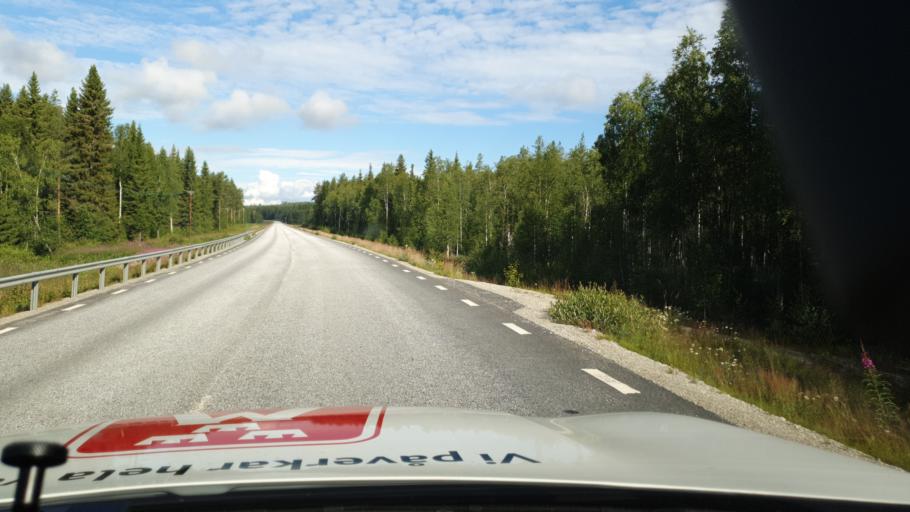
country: SE
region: Vaesterbotten
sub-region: Vannas Kommun
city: Vaennaes
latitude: 64.0450
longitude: 19.6855
